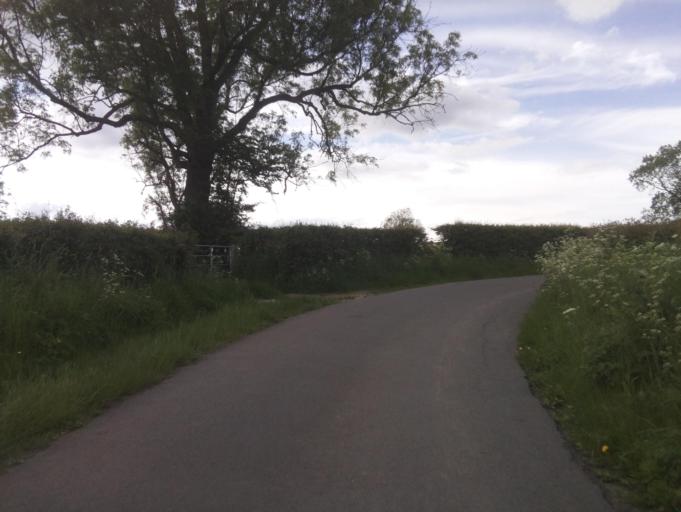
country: GB
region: England
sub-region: Gloucestershire
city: Moreton in Marsh
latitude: 52.0322
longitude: -1.7215
